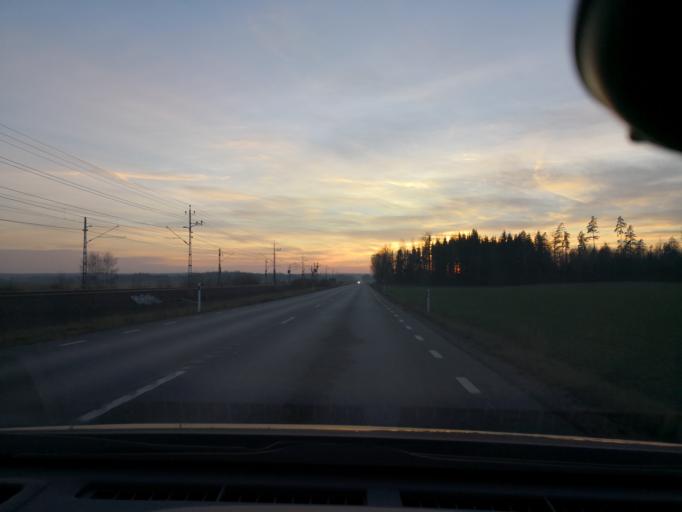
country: SE
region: Vaestmanland
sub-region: Arboga Kommun
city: Arboga
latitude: 59.4275
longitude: 15.9264
